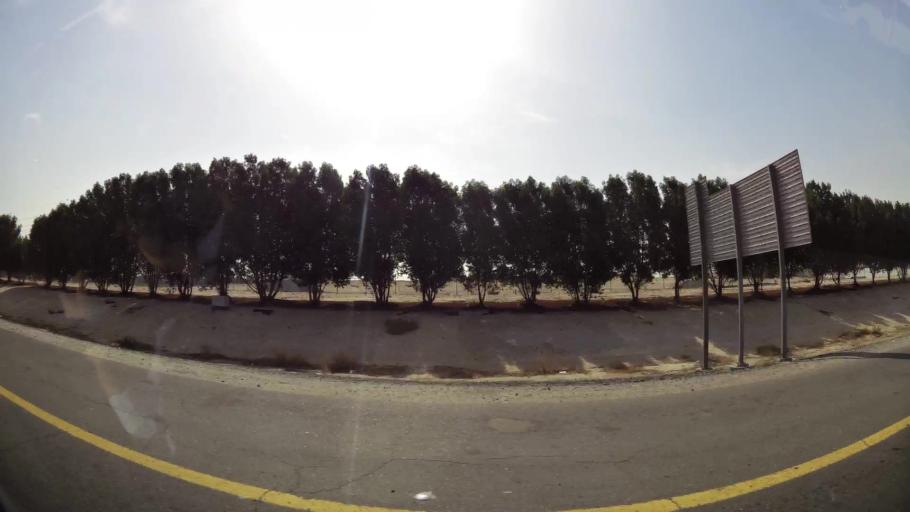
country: AE
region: Ash Shariqah
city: Sharjah
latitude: 25.2418
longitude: 55.4048
